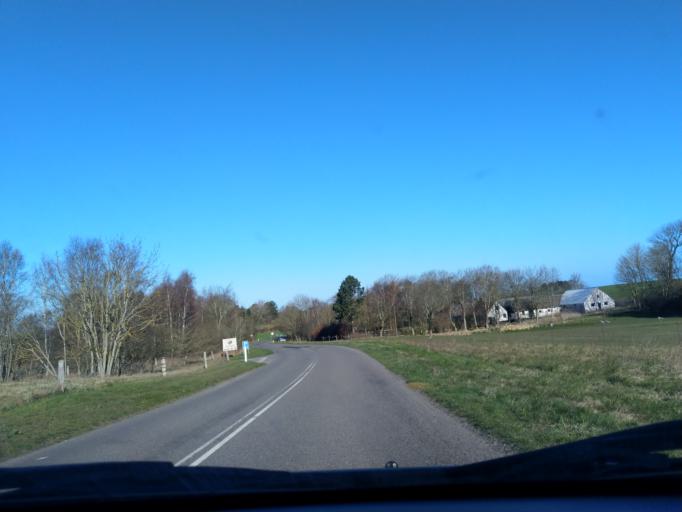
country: DK
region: Zealand
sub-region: Kalundborg Kommune
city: Kalundborg
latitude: 55.7231
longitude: 11.0054
